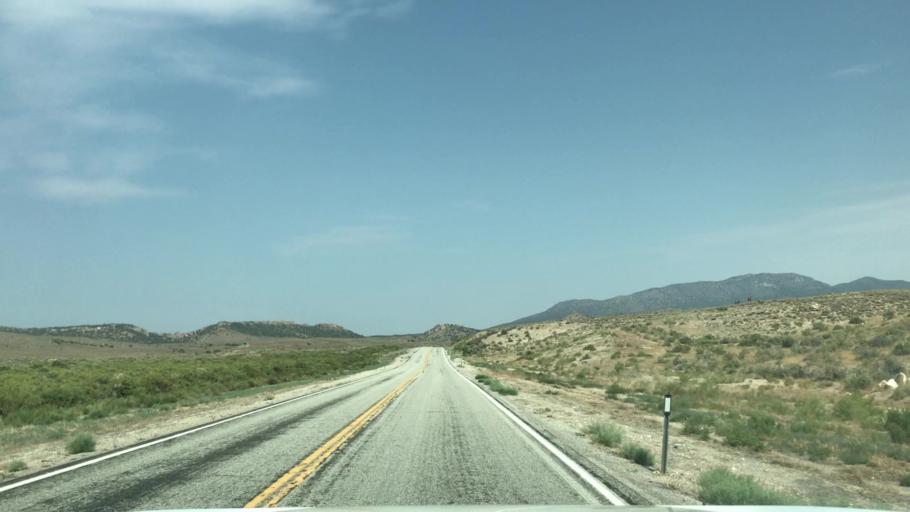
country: US
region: Nevada
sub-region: White Pine County
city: McGill
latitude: 39.1022
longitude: -114.2544
